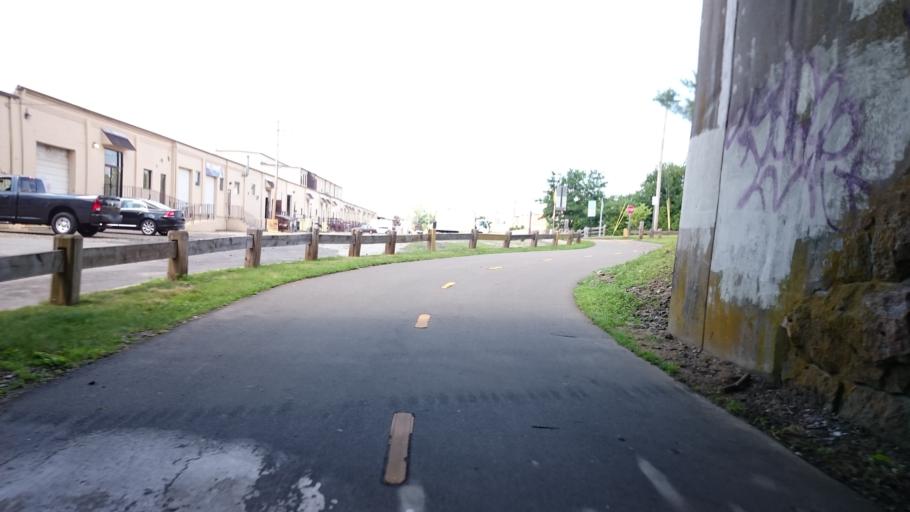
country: US
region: Connecticut
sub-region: New Haven County
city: New Haven
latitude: 41.3531
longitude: -72.9271
